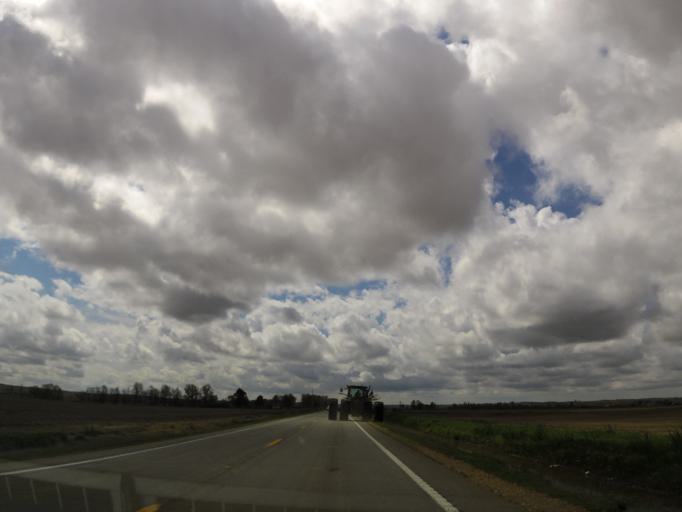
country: US
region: Arkansas
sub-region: Clay County
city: Corning
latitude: 36.2599
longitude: -90.5349
